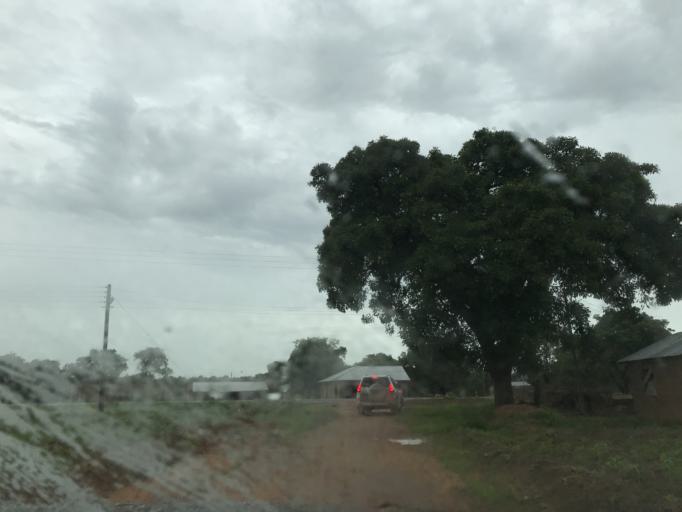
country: GH
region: Upper West
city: Wa
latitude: 10.5134
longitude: -2.6965
